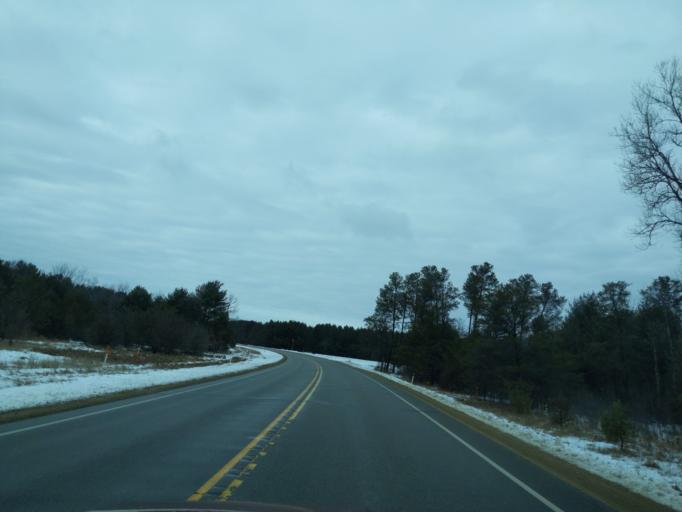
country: US
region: Wisconsin
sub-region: Waushara County
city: Wautoma
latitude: 43.9567
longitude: -89.3177
